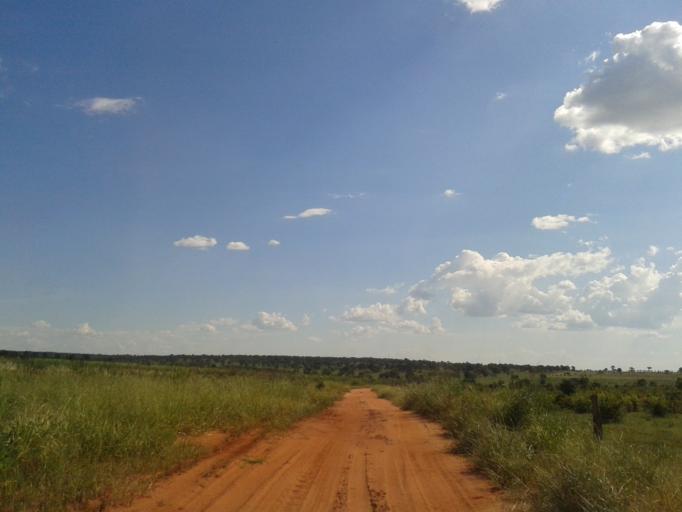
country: BR
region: Minas Gerais
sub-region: Santa Vitoria
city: Santa Vitoria
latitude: -19.1249
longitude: -50.4838
